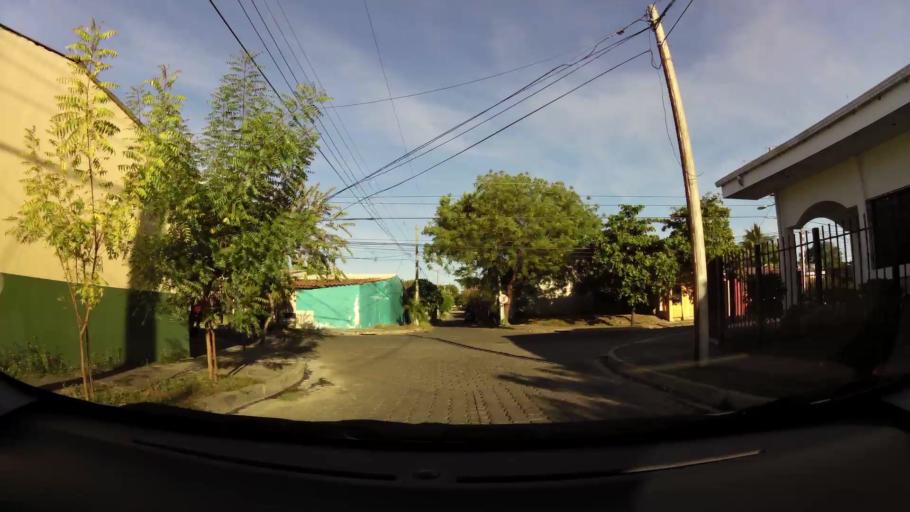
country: SV
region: San Miguel
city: San Miguel
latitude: 13.4566
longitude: -88.1616
